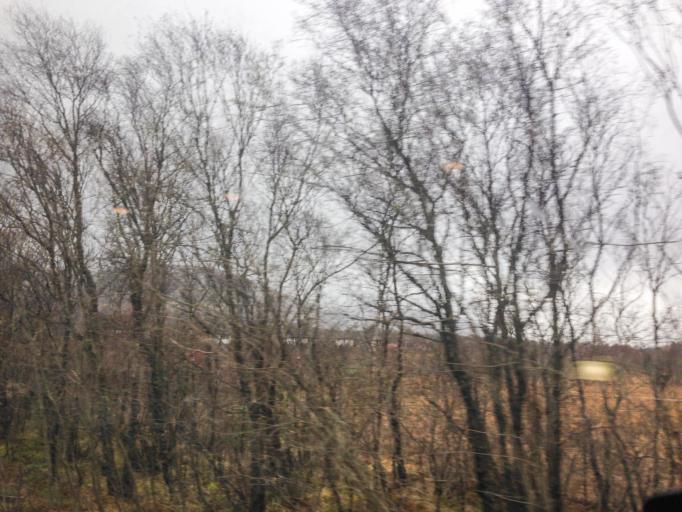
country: GB
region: Scotland
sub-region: Highland
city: Fort William
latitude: 56.8396
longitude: -5.0897
